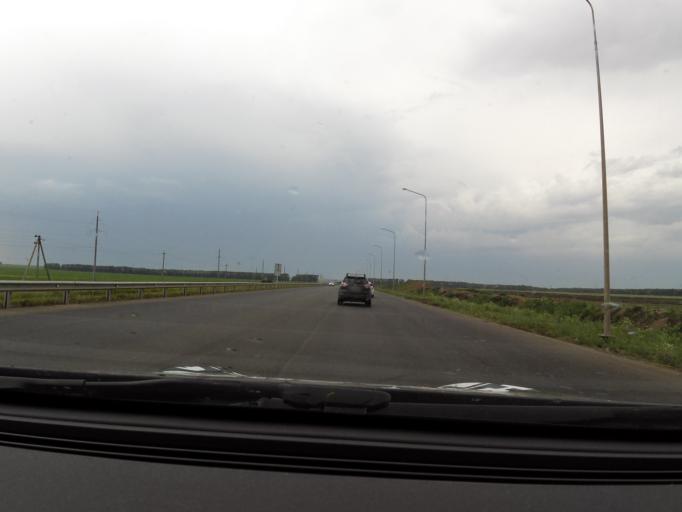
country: RU
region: Bashkortostan
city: Asanovo
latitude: 54.8842
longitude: 55.6856
